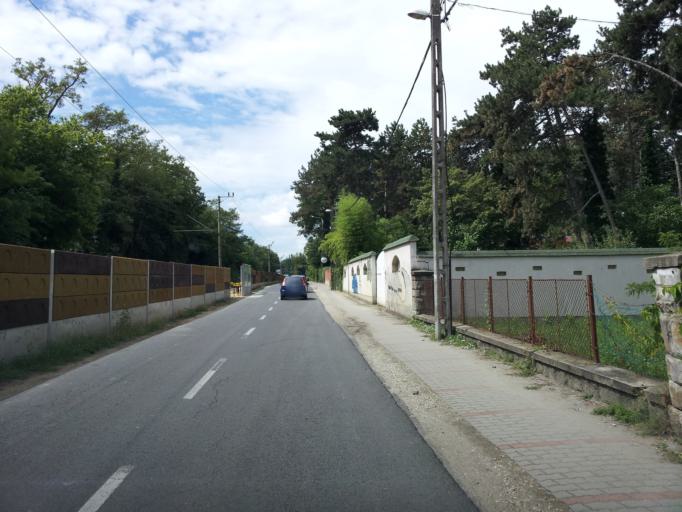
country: HU
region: Somogy
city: Balatonszabadi
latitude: 46.9273
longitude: 18.1057
